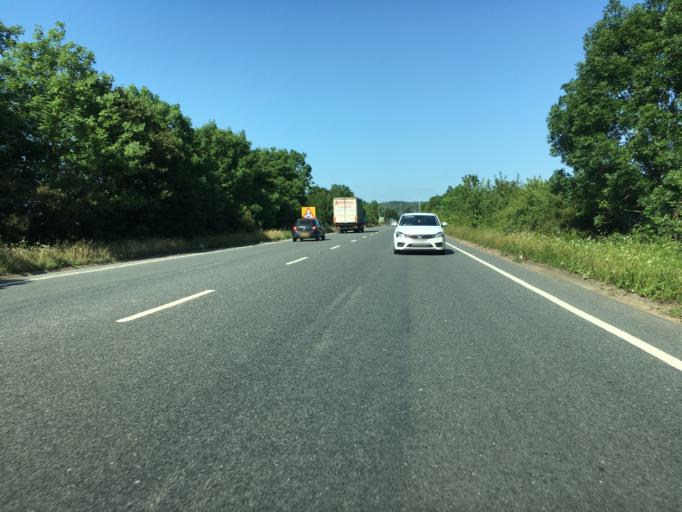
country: GB
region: England
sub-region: Milton Keynes
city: Water Eaton
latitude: 51.9823
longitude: -0.7057
